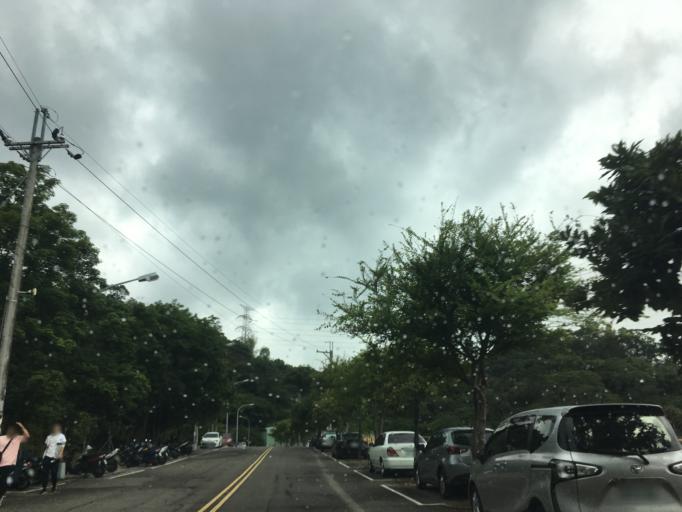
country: TW
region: Taiwan
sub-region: Taichung City
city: Taichung
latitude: 24.0680
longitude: 120.7167
